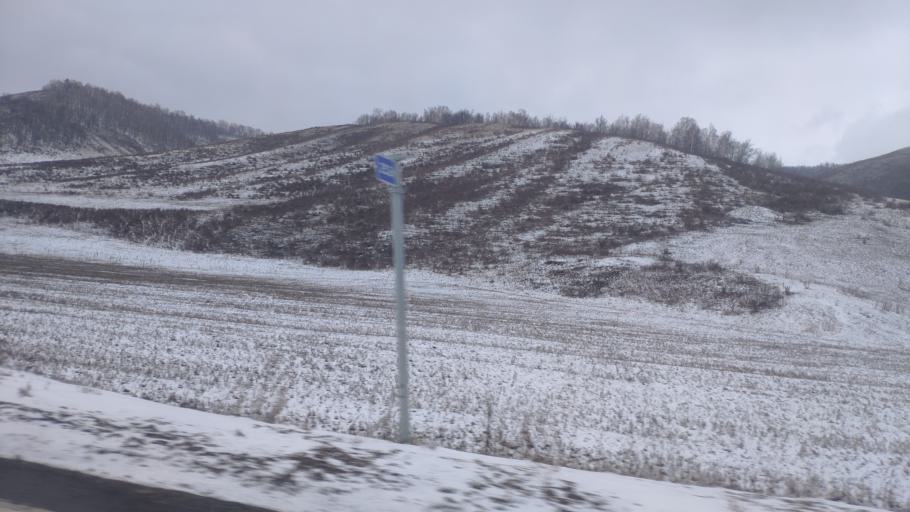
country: RU
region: Bashkortostan
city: Isyangulovo
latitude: 52.1619
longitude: 56.9046
